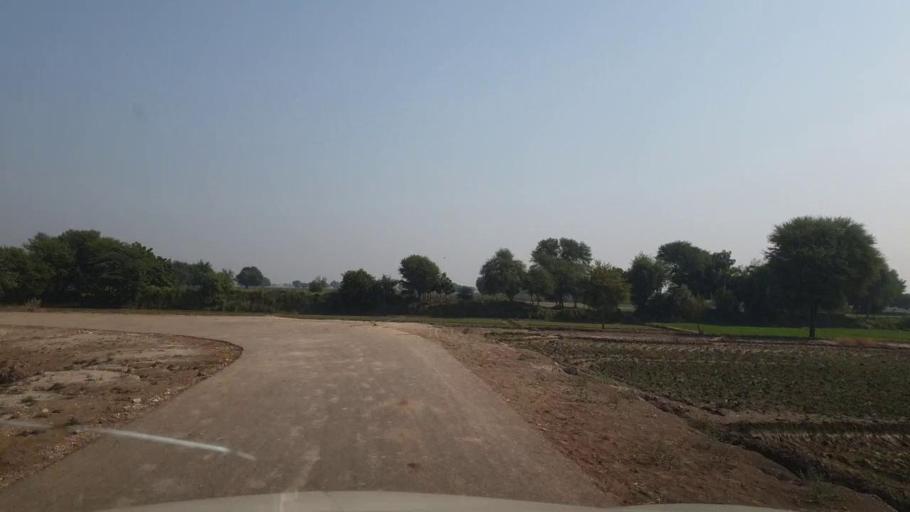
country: PK
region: Sindh
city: Bhan
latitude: 26.4874
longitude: 67.7813
